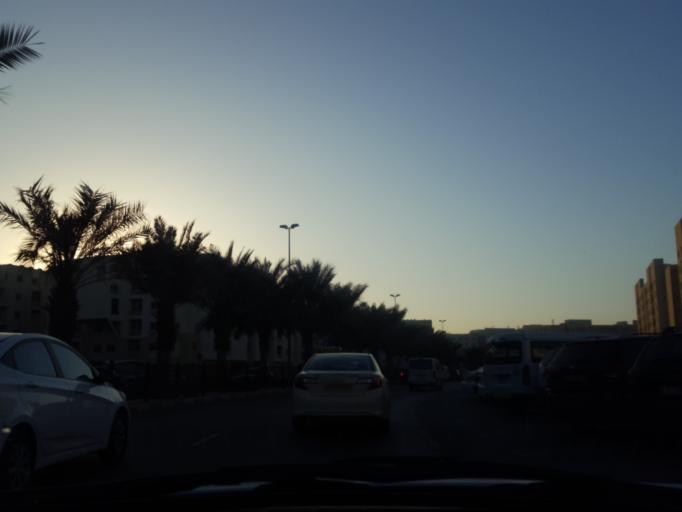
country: AE
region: Dubai
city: Dubai
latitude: 25.1418
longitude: 55.2525
